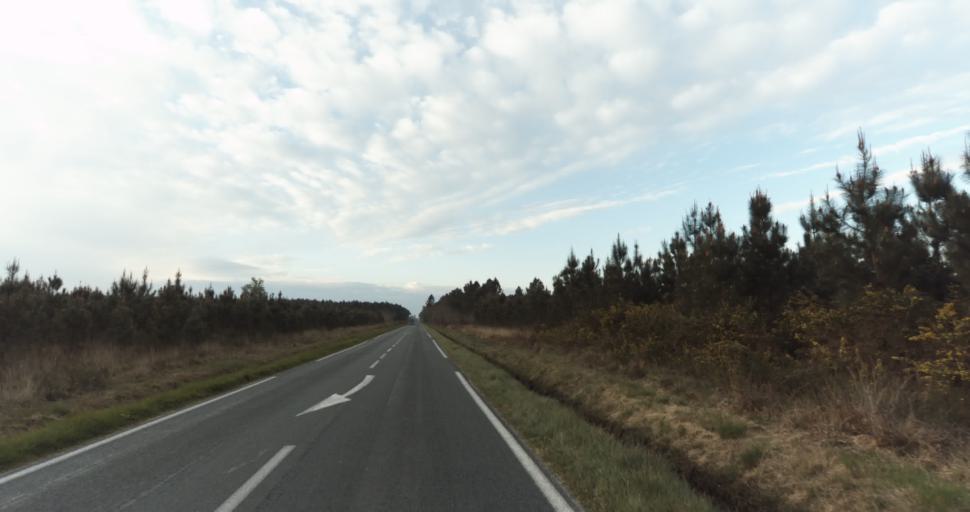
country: FR
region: Aquitaine
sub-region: Departement de la Gironde
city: Martignas-sur-Jalle
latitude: 44.7927
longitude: -0.7763
